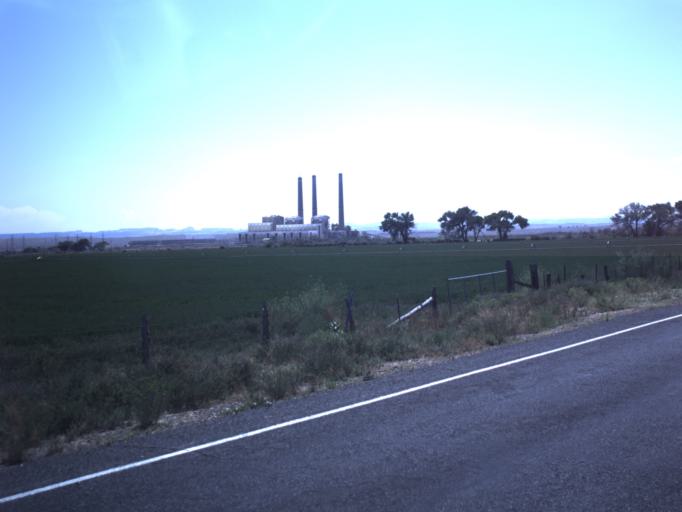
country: US
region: Utah
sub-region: Emery County
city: Castle Dale
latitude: 39.1908
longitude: -111.0477
